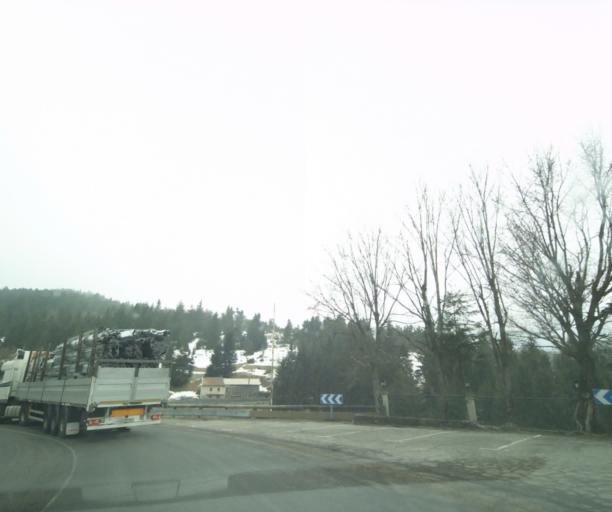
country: FR
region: Languedoc-Roussillon
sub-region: Departement de la Lozere
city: Langogne
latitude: 44.7252
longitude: 4.0068
